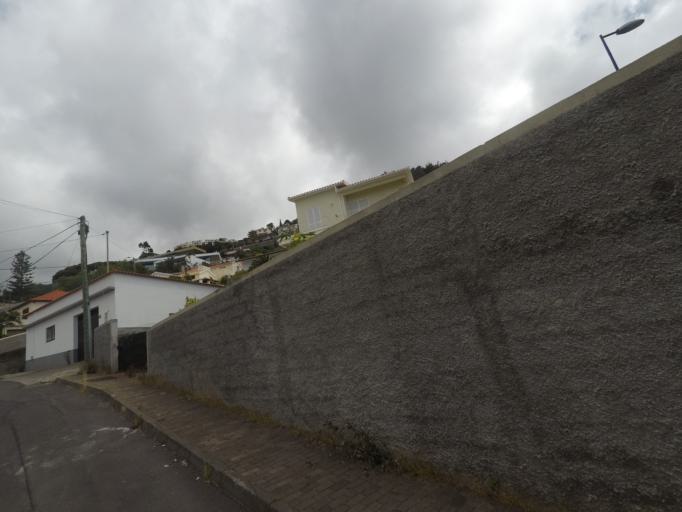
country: PT
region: Madeira
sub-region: Funchal
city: Nossa Senhora do Monte
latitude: 32.6505
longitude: -16.8778
